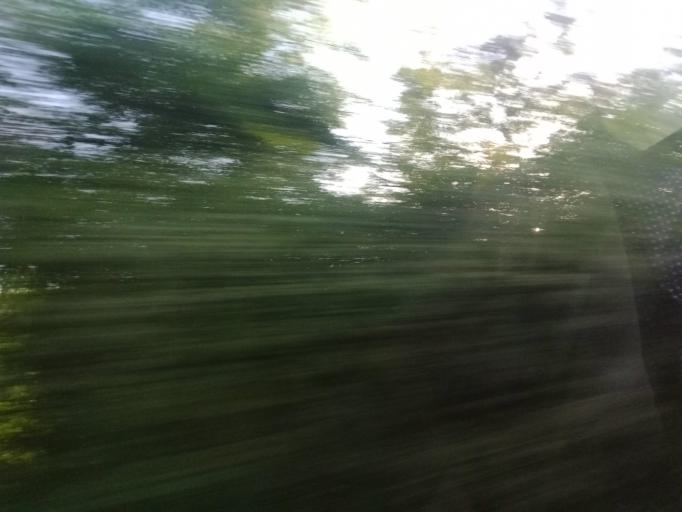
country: IE
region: Leinster
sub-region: Kilkenny
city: Kilkenny
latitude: 52.7253
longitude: -7.2370
